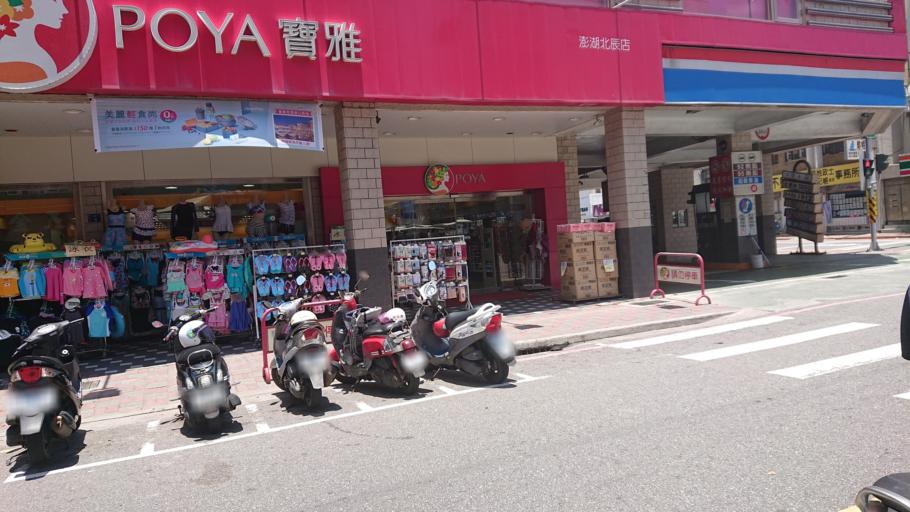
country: TW
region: Taiwan
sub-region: Penghu
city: Ma-kung
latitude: 23.5704
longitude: 119.5713
